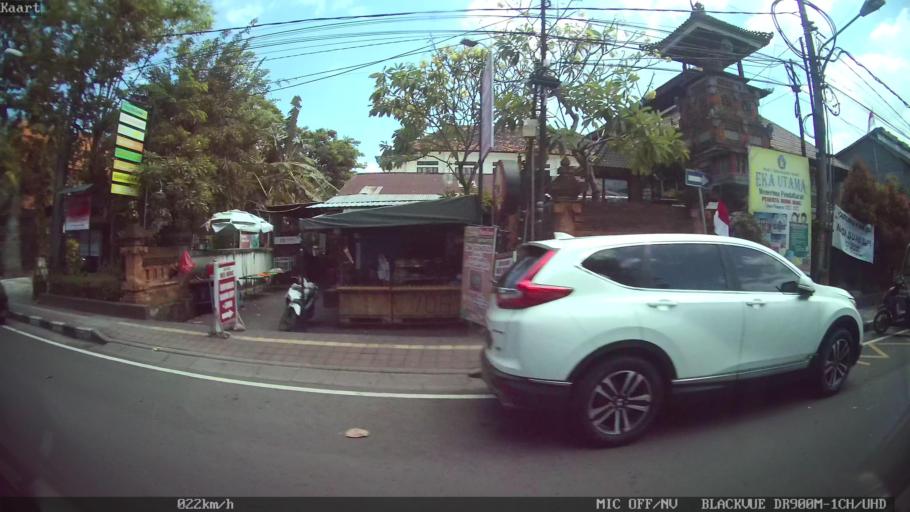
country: ID
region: Bali
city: Denpasar
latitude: -8.6597
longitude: 115.2092
